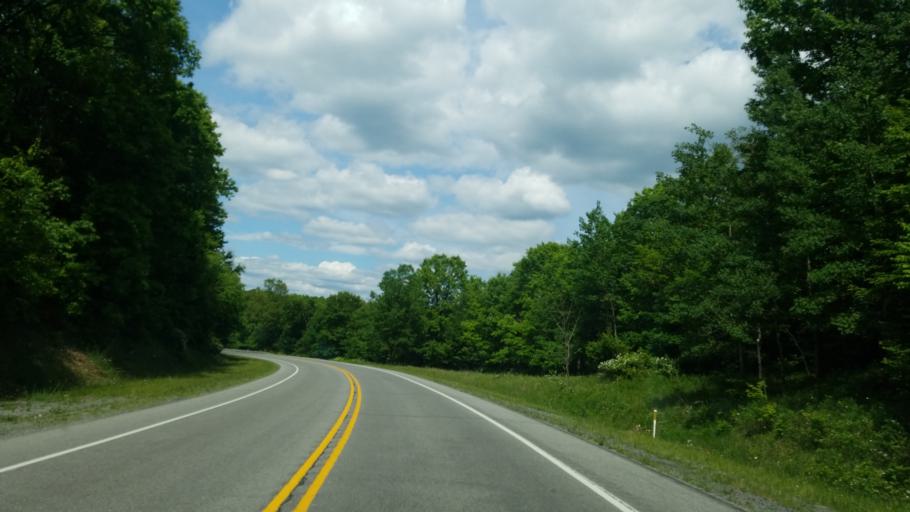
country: US
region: Pennsylvania
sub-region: Clearfield County
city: Hyde
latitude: 40.9376
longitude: -78.3775
